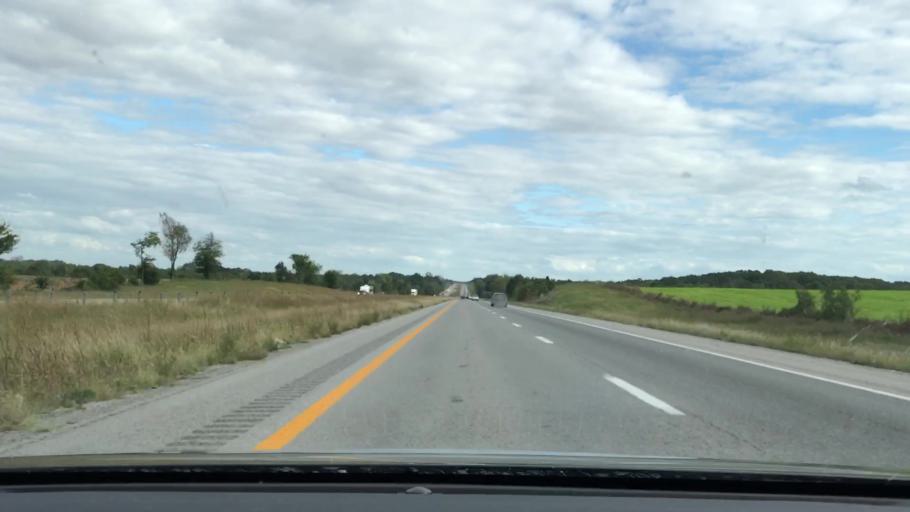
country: US
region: Kentucky
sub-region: Christian County
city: Hopkinsville
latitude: 36.7694
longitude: -87.5546
